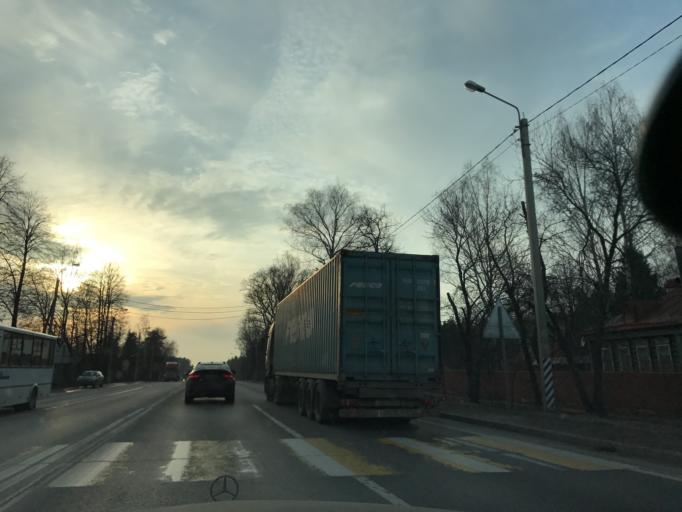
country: RU
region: Vladimir
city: Petushki
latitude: 55.9280
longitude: 39.3194
